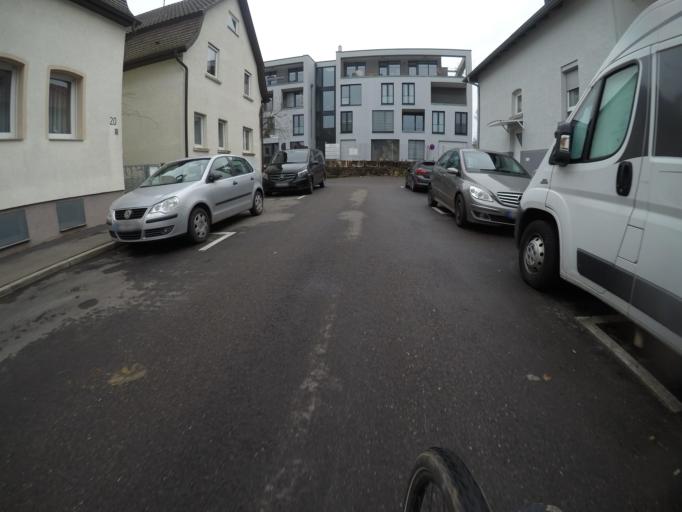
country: DE
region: Baden-Wuerttemberg
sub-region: Regierungsbezirk Stuttgart
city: Waiblingen
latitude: 48.8276
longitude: 9.3097
